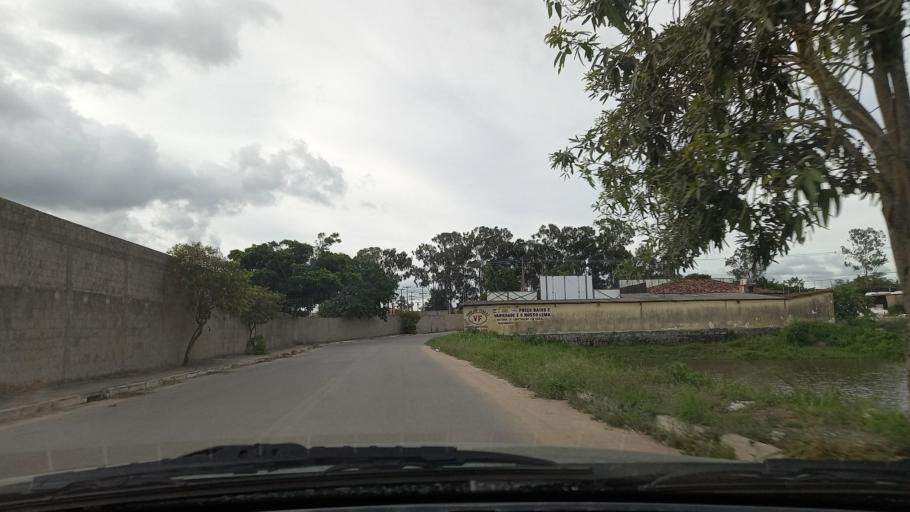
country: BR
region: Pernambuco
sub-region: Gravata
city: Gravata
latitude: -8.1953
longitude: -35.5411
